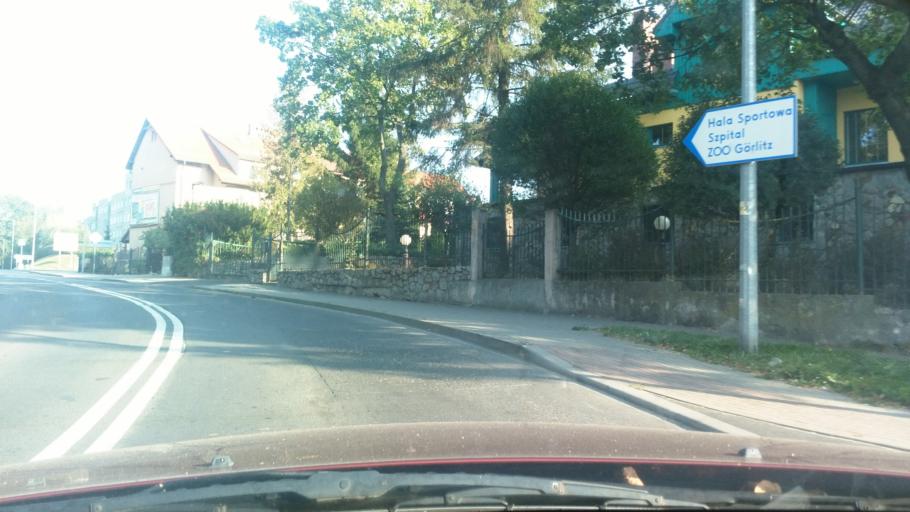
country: DE
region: Saxony
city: Goerlitz
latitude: 51.1596
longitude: 14.9991
